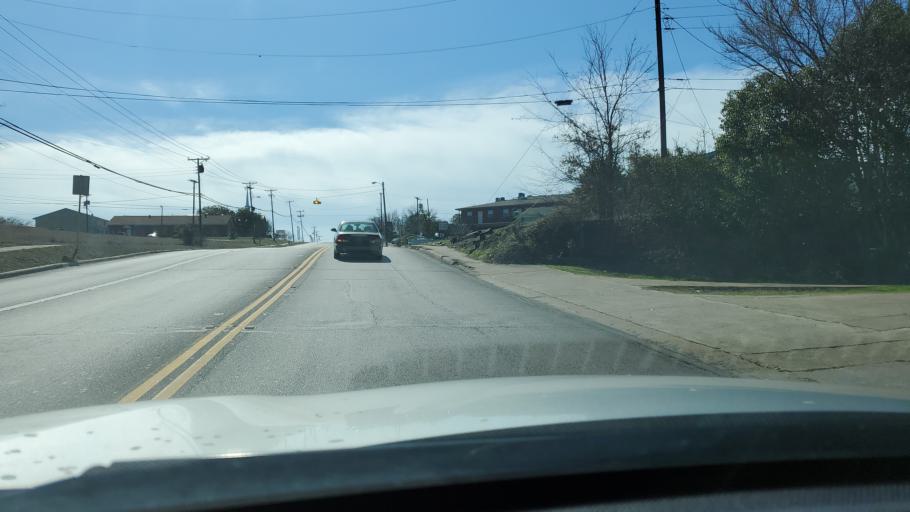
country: US
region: Texas
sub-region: Bell County
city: Killeen
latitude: 31.1109
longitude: -97.7287
